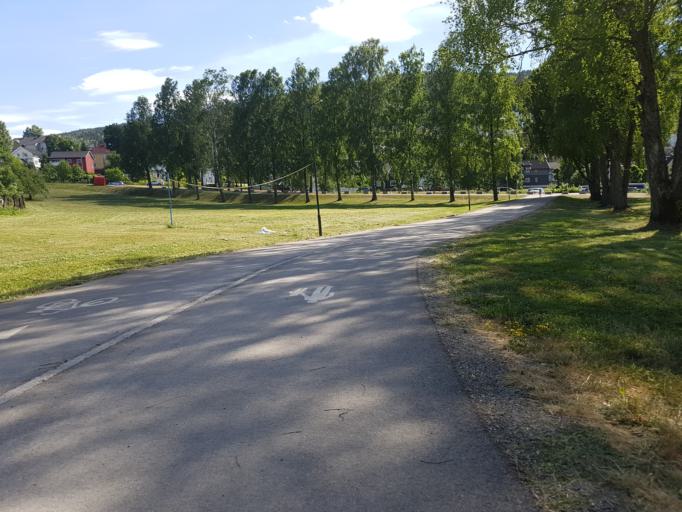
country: NO
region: Buskerud
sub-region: Drammen
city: Drammen
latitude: 59.7401
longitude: 10.1829
